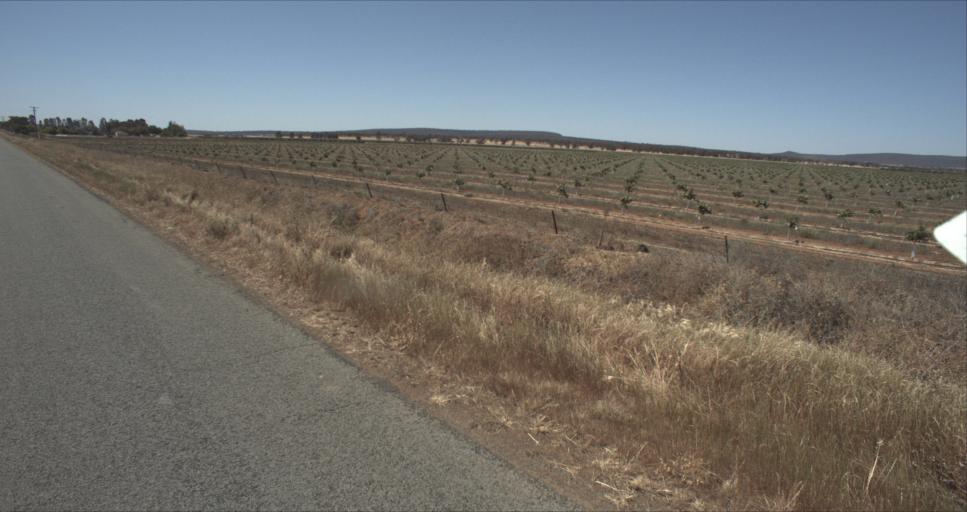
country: AU
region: New South Wales
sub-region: Leeton
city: Leeton
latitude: -34.4894
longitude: 146.4136
